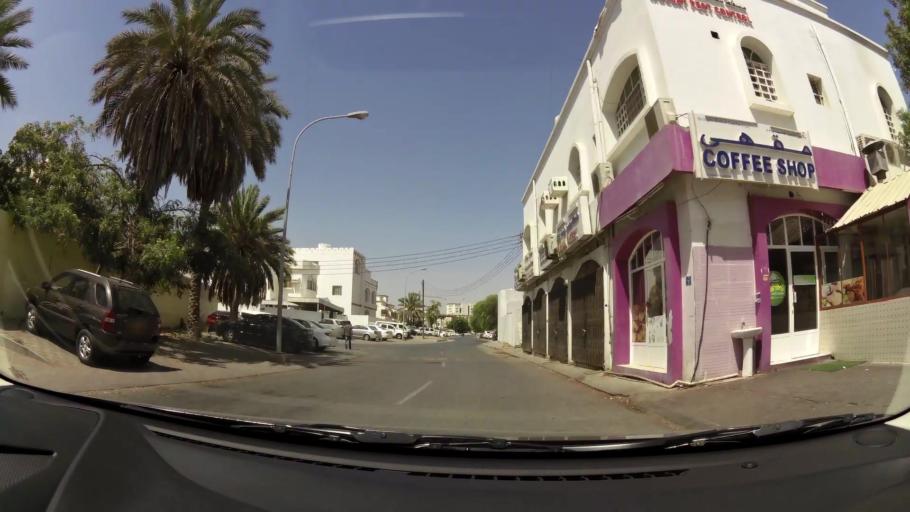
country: OM
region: Muhafazat Masqat
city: Bawshar
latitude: 23.5874
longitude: 58.4010
